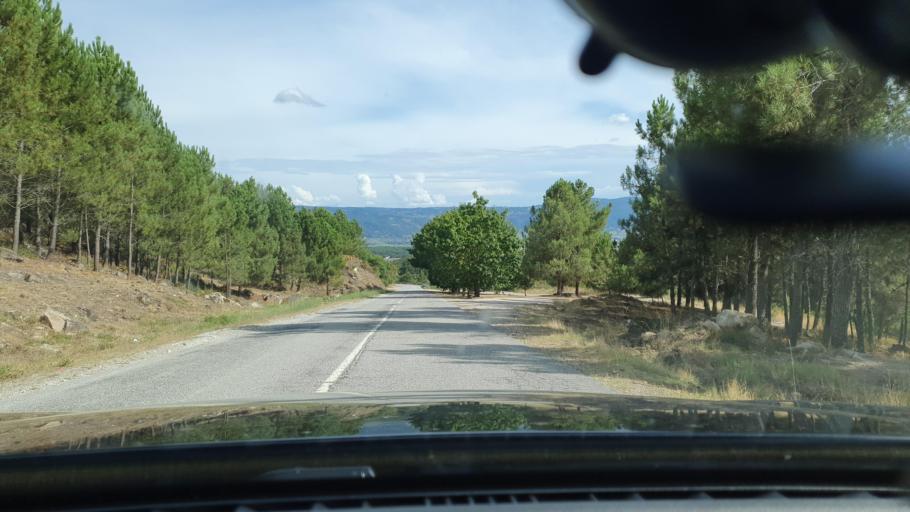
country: PT
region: Vila Real
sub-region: Chaves
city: Chaves
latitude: 41.7908
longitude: -7.5064
